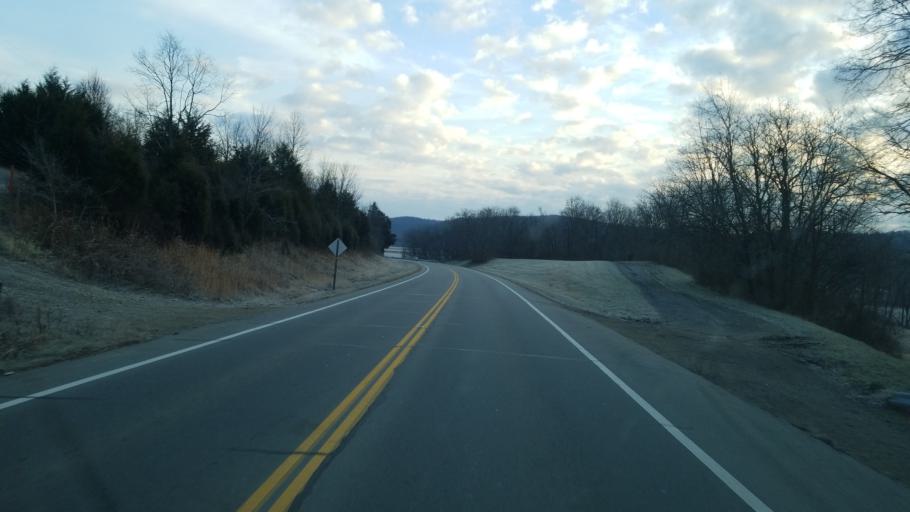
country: US
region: Ohio
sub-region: Ross County
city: North Fork Village
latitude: 39.3121
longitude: -83.1170
